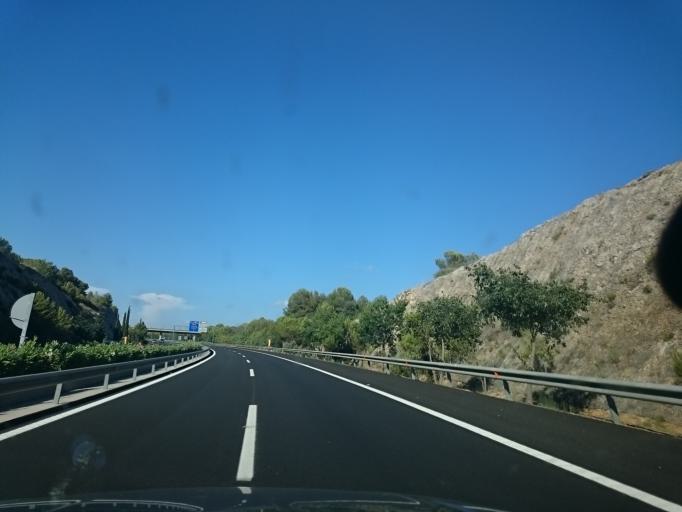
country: ES
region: Catalonia
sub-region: Provincia de Barcelona
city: Cubelles
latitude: 41.2155
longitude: 1.6701
